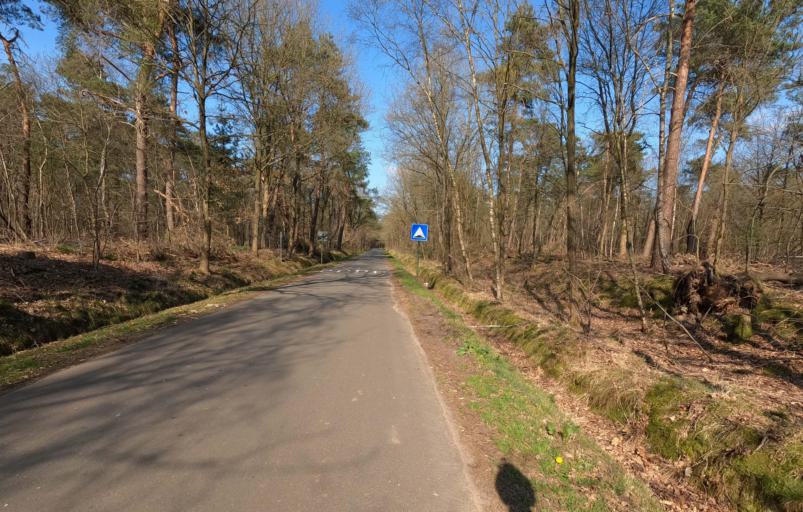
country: BE
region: Flanders
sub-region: Provincie Antwerpen
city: Merksplas
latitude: 51.3850
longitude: 4.8682
